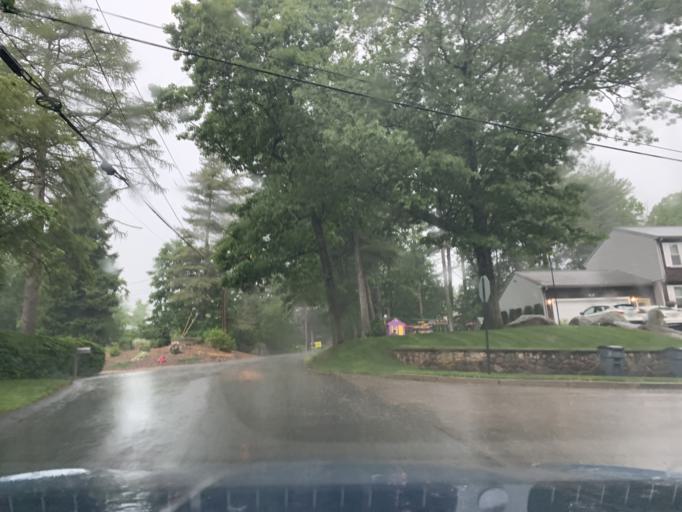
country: US
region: Rhode Island
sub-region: Kent County
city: West Warwick
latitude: 41.7286
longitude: -71.5557
